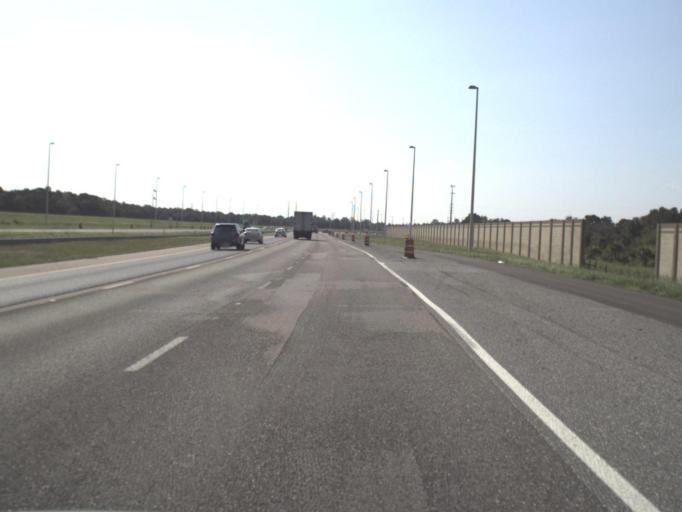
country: US
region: Florida
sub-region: Hillsborough County
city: Pebble Creek
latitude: 28.0983
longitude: -82.3635
